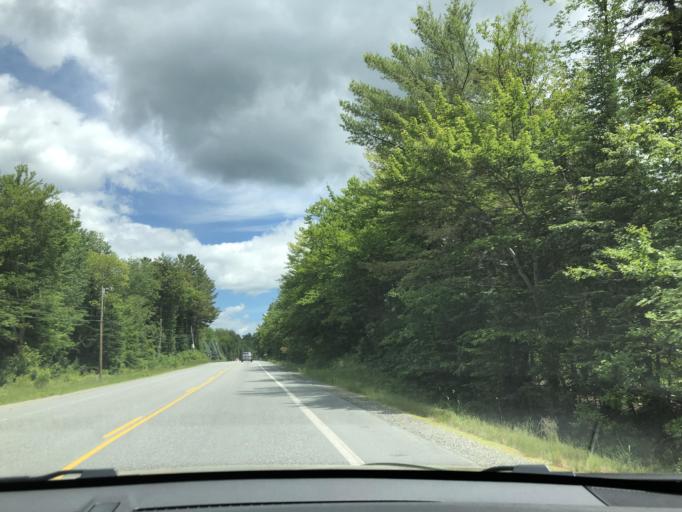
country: US
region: New Hampshire
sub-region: Merrimack County
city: New London
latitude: 43.4269
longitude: -72.0147
